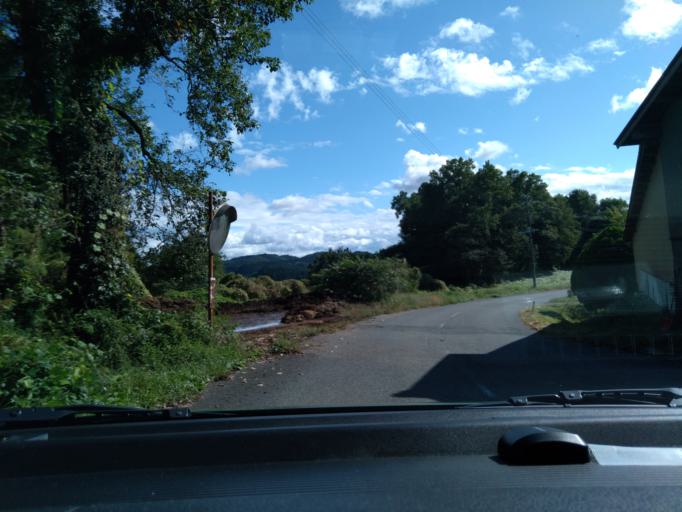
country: JP
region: Iwate
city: Ichinoseki
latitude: 38.7811
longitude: 141.2066
